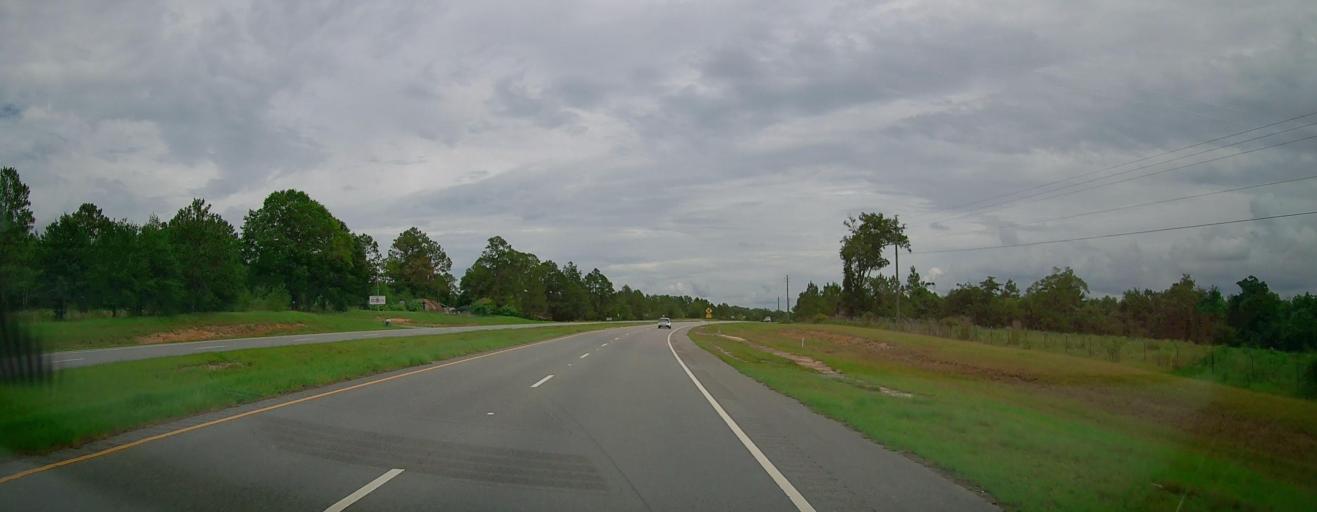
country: US
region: Georgia
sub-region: Telfair County
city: Helena
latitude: 32.1033
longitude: -82.9625
